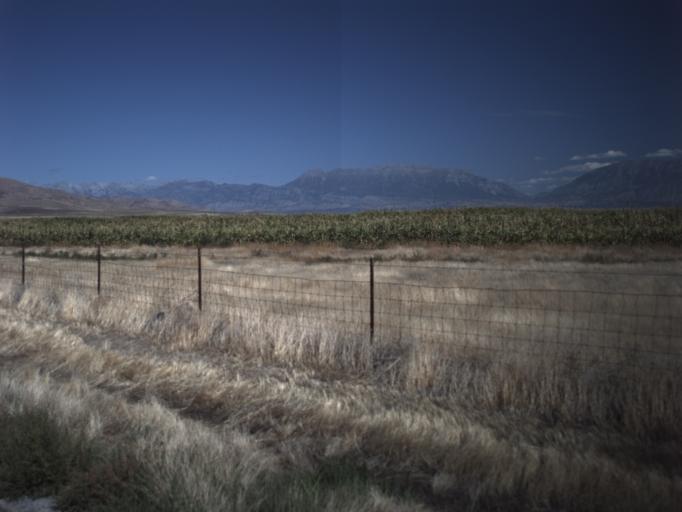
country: US
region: Utah
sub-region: Utah County
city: Genola
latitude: 40.1149
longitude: -111.9591
